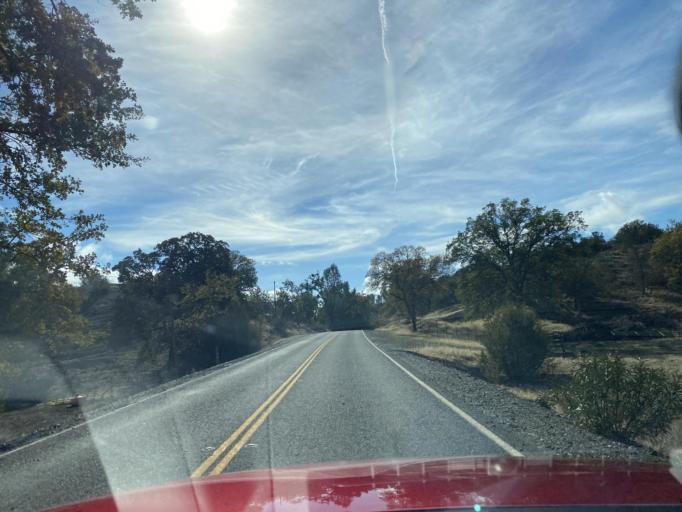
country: US
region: California
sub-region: Glenn County
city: Willows
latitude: 39.4488
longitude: -122.5136
